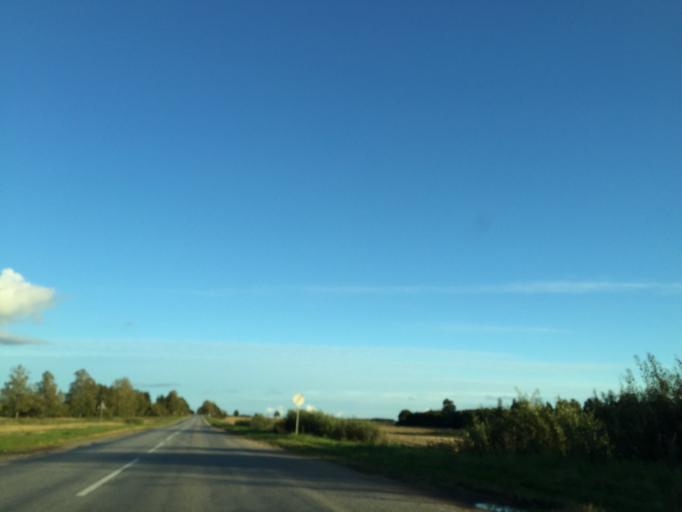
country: LV
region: Saldus Rajons
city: Saldus
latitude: 56.7253
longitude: 22.3821
